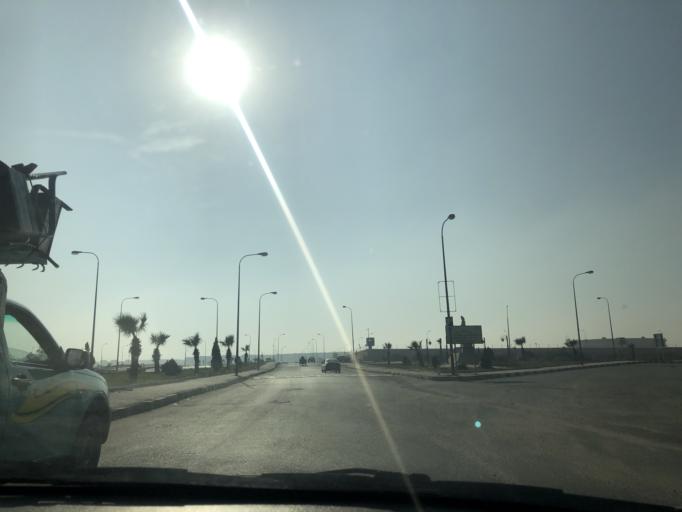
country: EG
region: Al Jizah
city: Madinat Sittah Uktubar
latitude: 29.9332
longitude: 31.0437
